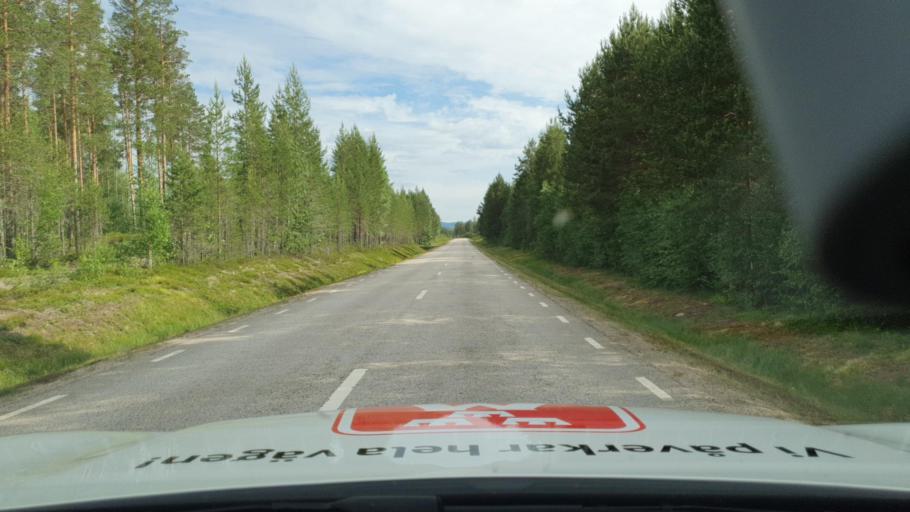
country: NO
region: Hedmark
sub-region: Trysil
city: Innbygda
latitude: 60.9524
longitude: 12.4677
